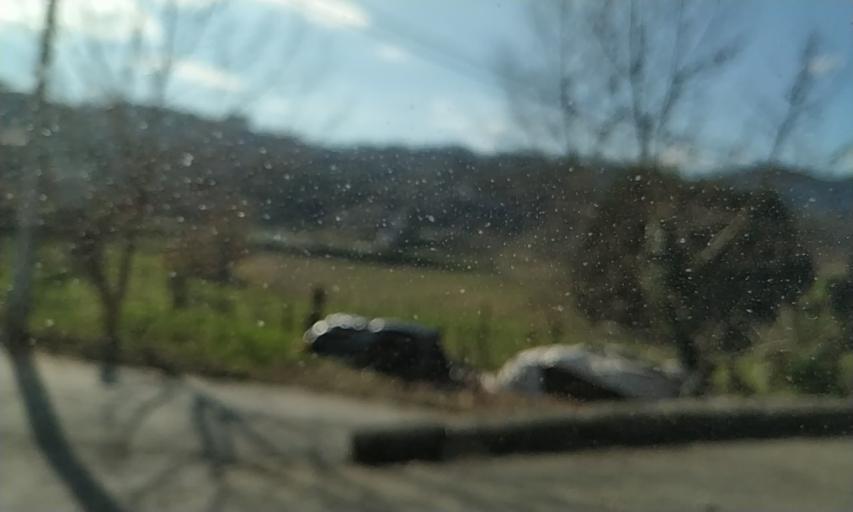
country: PT
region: Vila Real
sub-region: Mondim de Basto
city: Mondim de Basto
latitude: 41.4143
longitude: -7.9777
